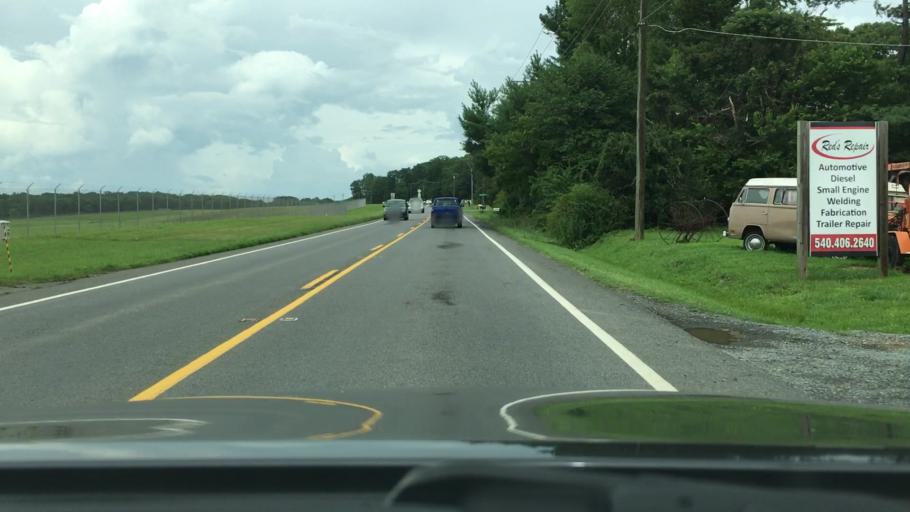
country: US
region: Virginia
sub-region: Orange County
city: Orange
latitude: 38.2463
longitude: -78.0435
